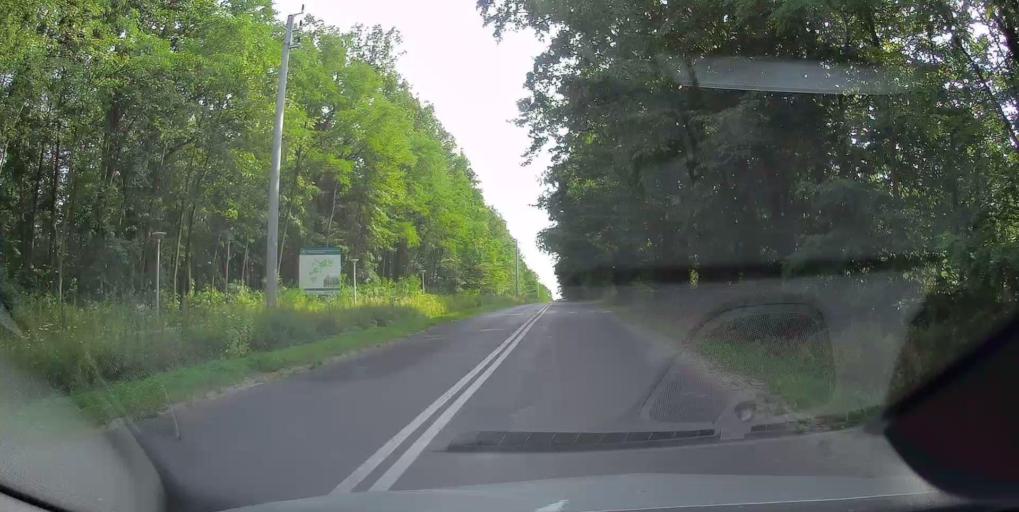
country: PL
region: Lodz Voivodeship
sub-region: Powiat tomaszowski
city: Tomaszow Mazowiecki
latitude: 51.5144
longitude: 20.0008
